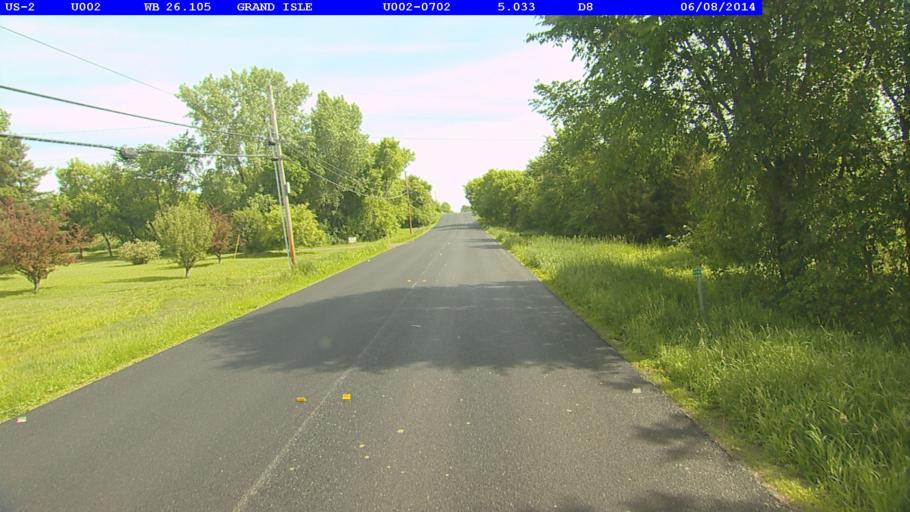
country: US
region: New York
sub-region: Clinton County
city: Cumberland Head
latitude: 44.6965
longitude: -73.3056
